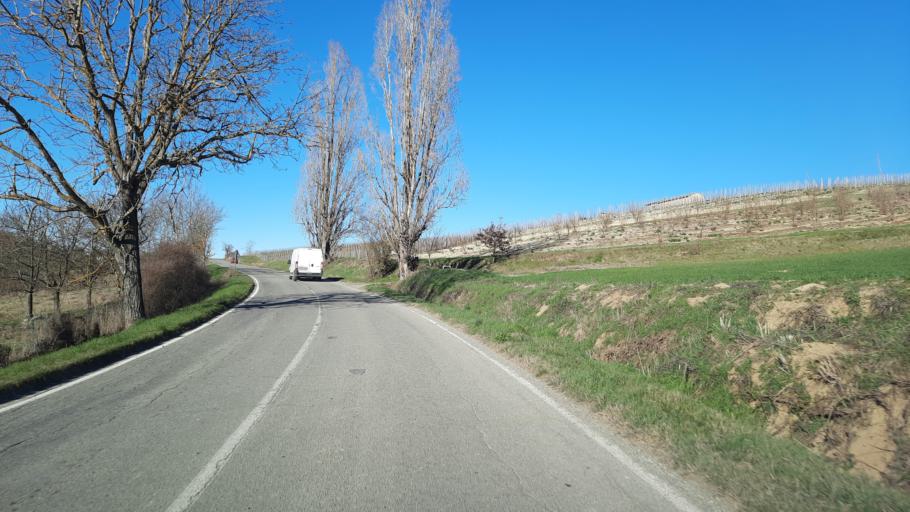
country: IT
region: Piedmont
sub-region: Provincia di Alessandria
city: Rosignano Monferrato
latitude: 45.0698
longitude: 8.4042
